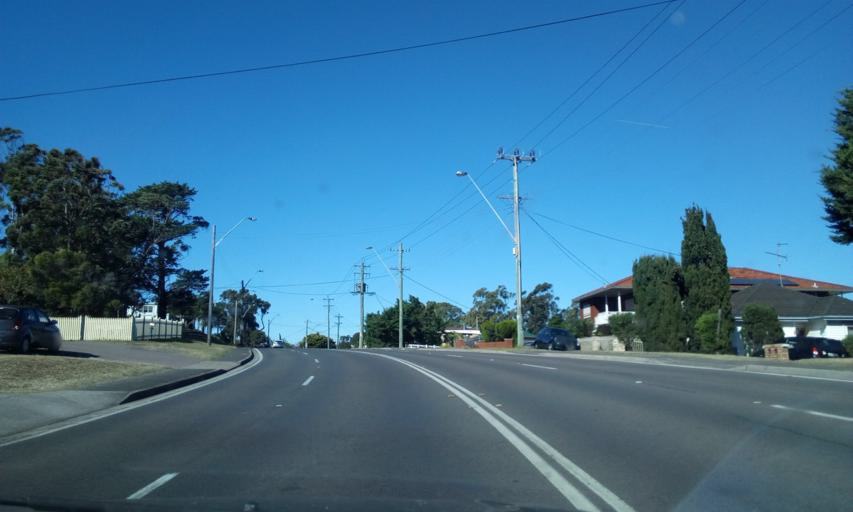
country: AU
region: New South Wales
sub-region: Wollongong
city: Dapto
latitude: -34.5081
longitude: 150.7859
